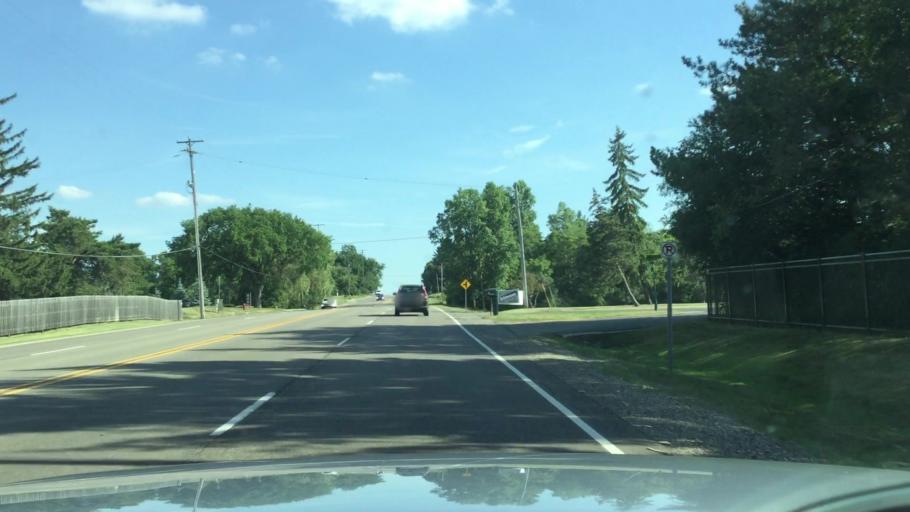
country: US
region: Michigan
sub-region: Genesee County
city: Grand Blanc
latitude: 42.9003
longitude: -83.6021
